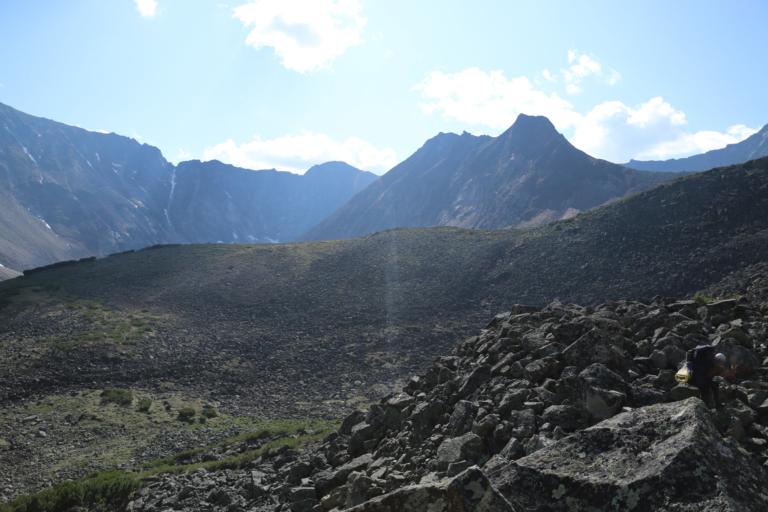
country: RU
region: Respublika Buryatiya
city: Novyy Uoyan
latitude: 56.3006
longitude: 111.2853
